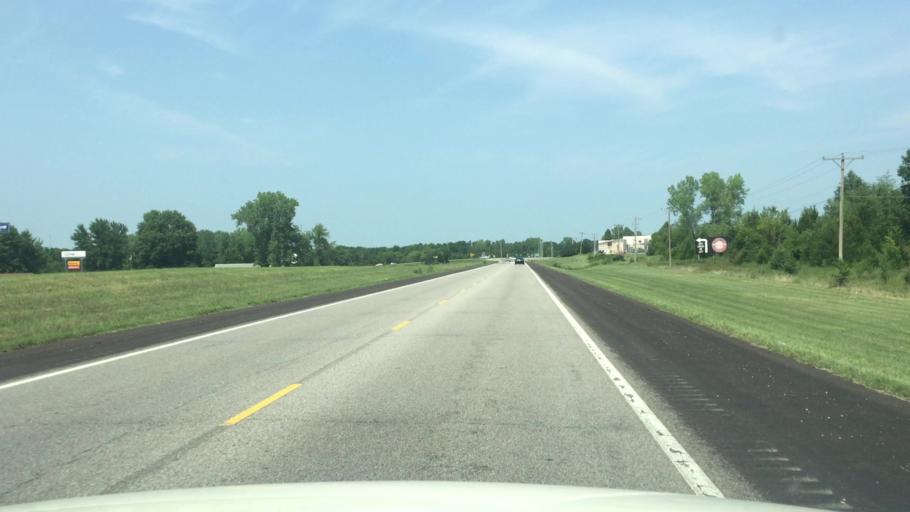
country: US
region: Kansas
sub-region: Crawford County
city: Pittsburg
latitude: 37.4345
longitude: -94.7108
